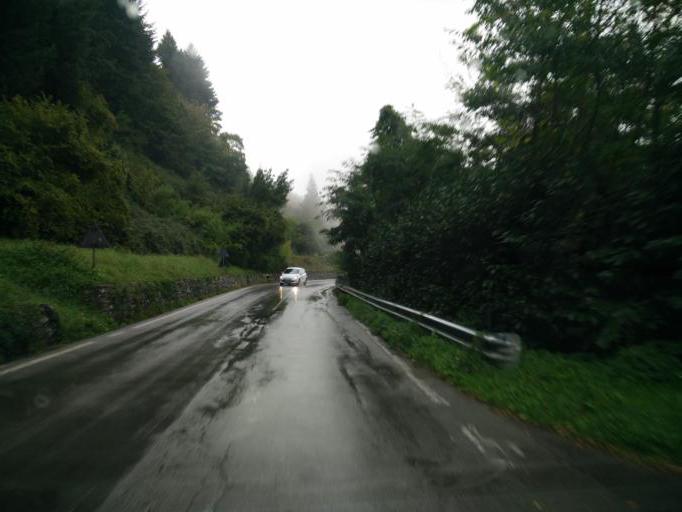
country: IT
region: Tuscany
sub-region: Provincia di Lucca
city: San Romano in Garfagnana
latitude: 44.1671
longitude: 10.3519
